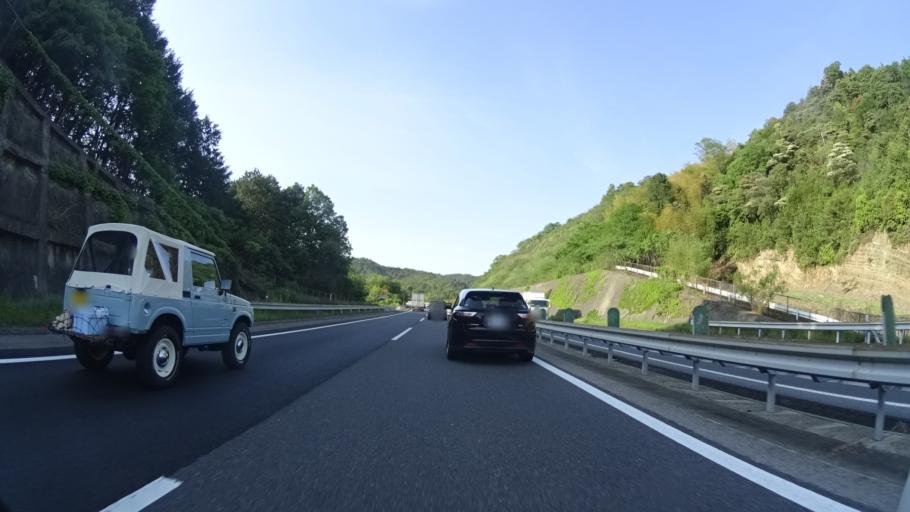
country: JP
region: Ehime
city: Kawanoecho
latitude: 34.0136
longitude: 133.6007
